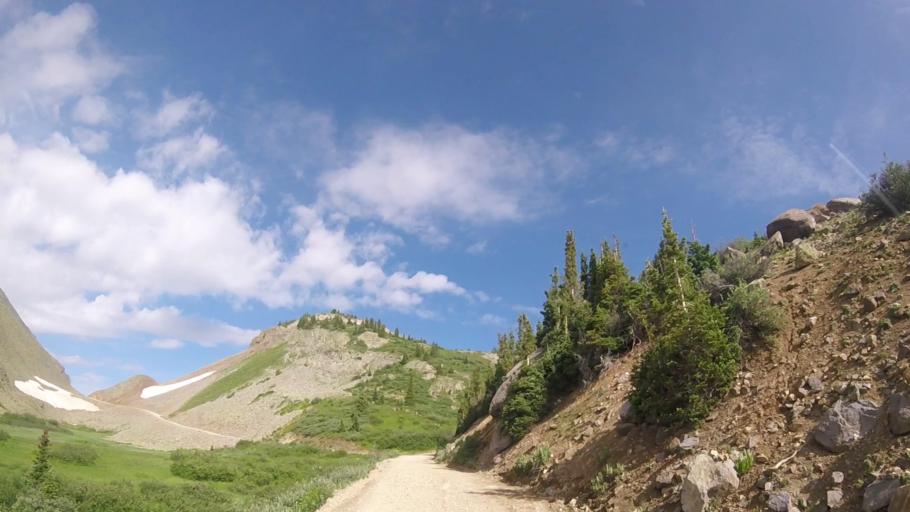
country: US
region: Colorado
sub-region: San Miguel County
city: Telluride
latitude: 37.8513
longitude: -107.7752
